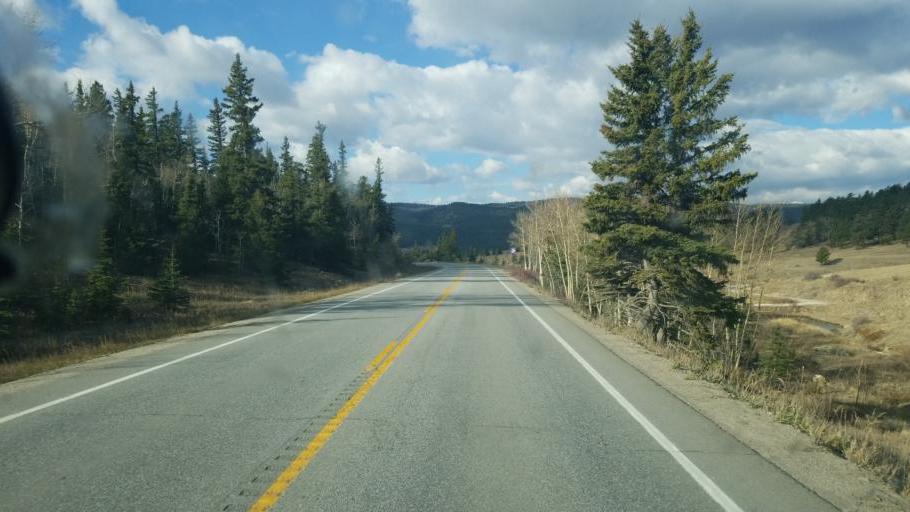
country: US
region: Colorado
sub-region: Chaffee County
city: Buena Vista
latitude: 38.9057
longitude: -105.9853
